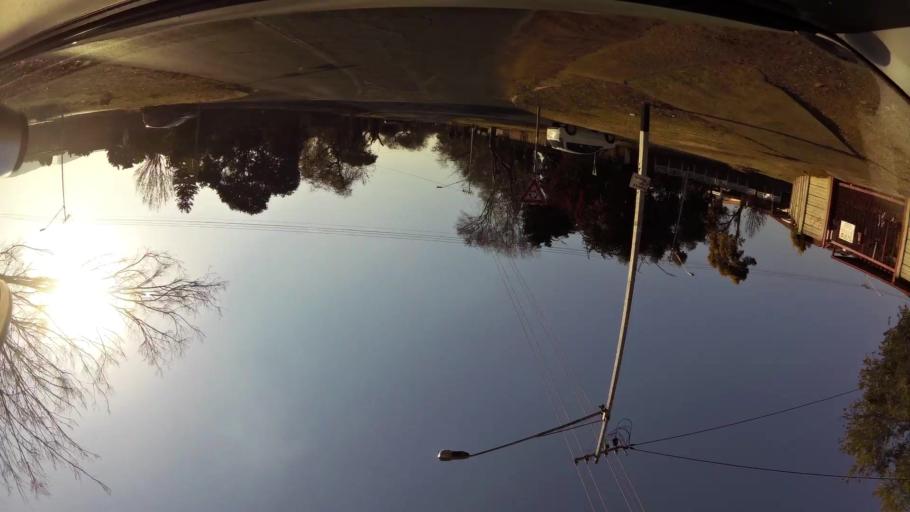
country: ZA
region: Gauteng
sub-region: City of Tshwane Metropolitan Municipality
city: Pretoria
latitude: -25.7601
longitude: 28.1153
